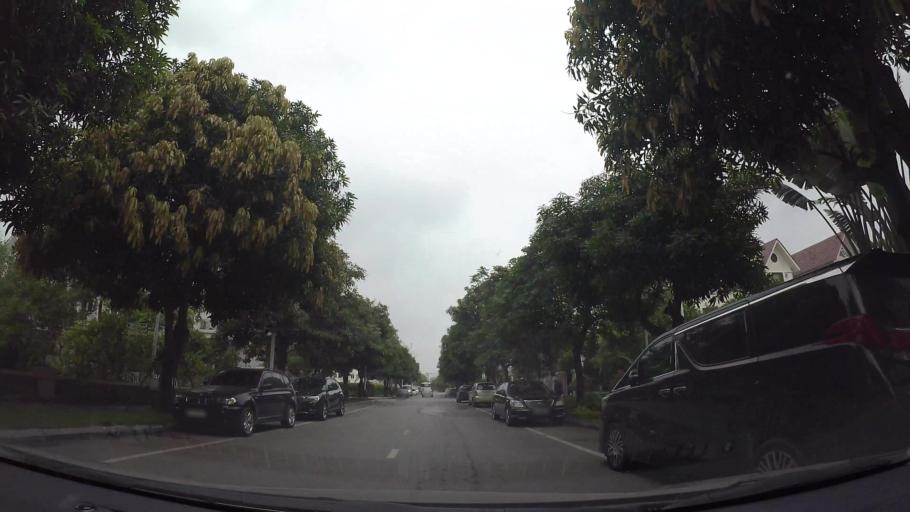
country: VN
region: Ha Noi
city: Trau Quy
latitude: 21.0429
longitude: 105.9204
